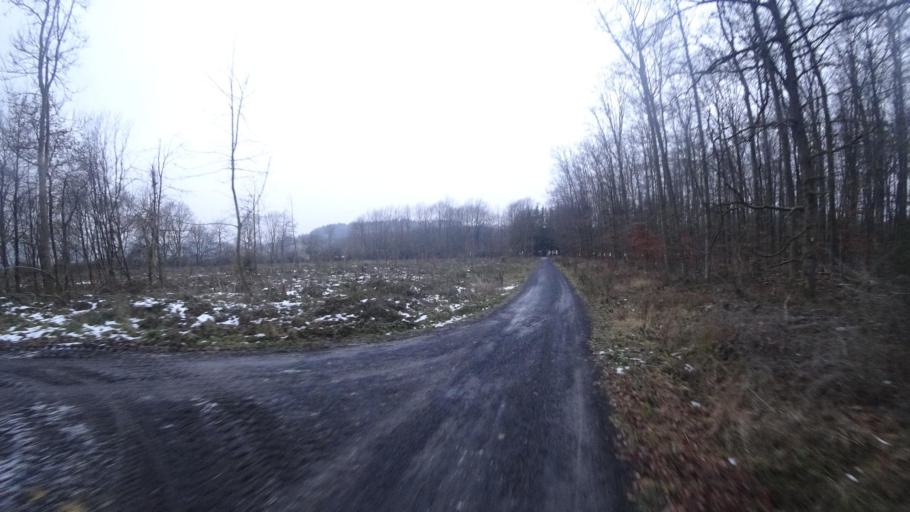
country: DE
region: Rheinland-Pfalz
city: Ailertchen
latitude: 50.6082
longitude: 7.9191
